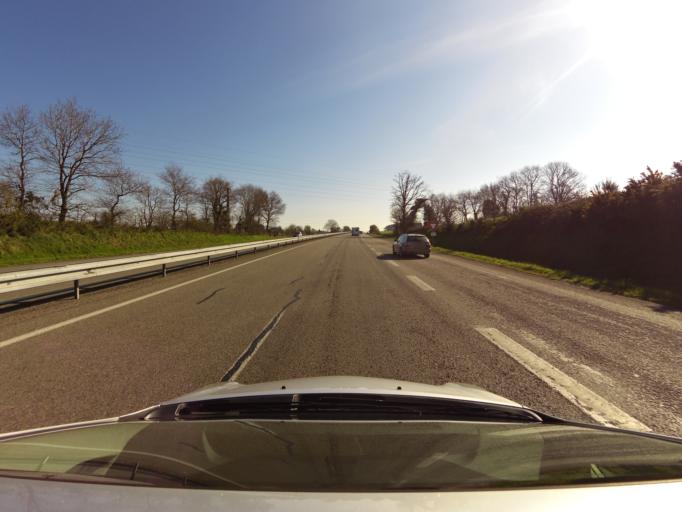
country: FR
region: Brittany
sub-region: Departement du Morbihan
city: Josselin
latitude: 47.9576
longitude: -2.5670
